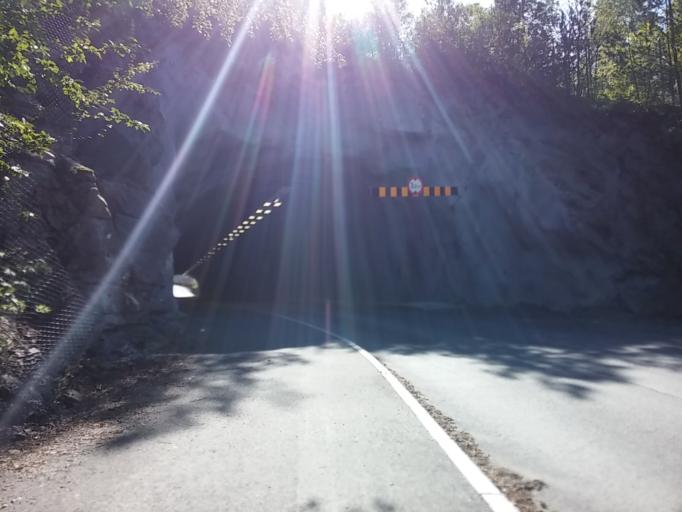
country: NO
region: Sor-Trondelag
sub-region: Malvik
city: Hommelvik
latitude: 63.4272
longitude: 10.7497
